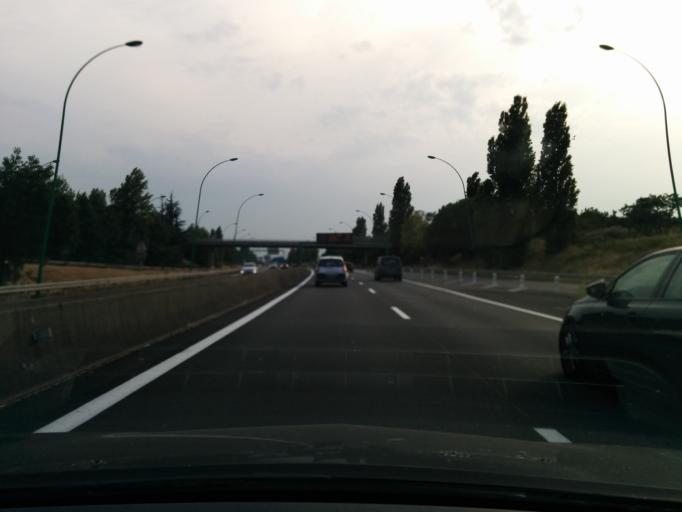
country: FR
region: Midi-Pyrenees
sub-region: Departement de la Haute-Garonne
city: L'Union
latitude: 43.6429
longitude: 1.4937
